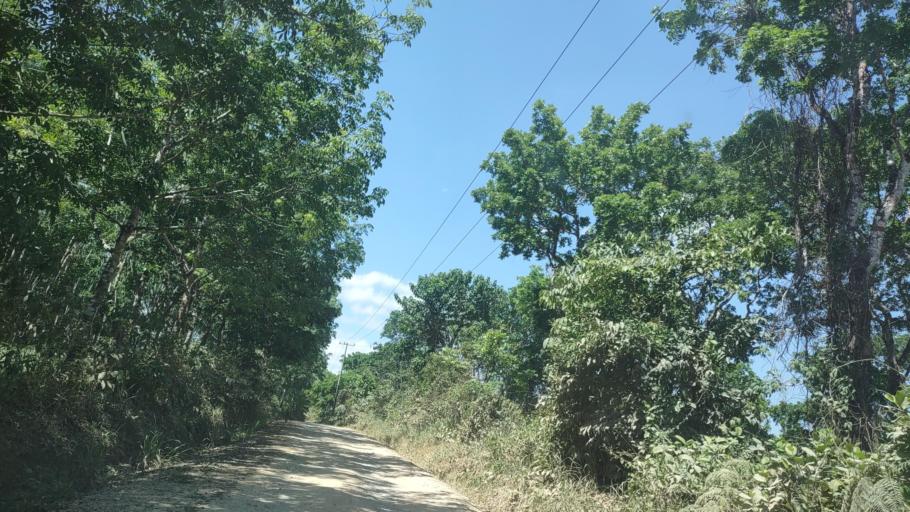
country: MX
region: Veracruz
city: Las Choapas
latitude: 17.7704
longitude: -94.1515
